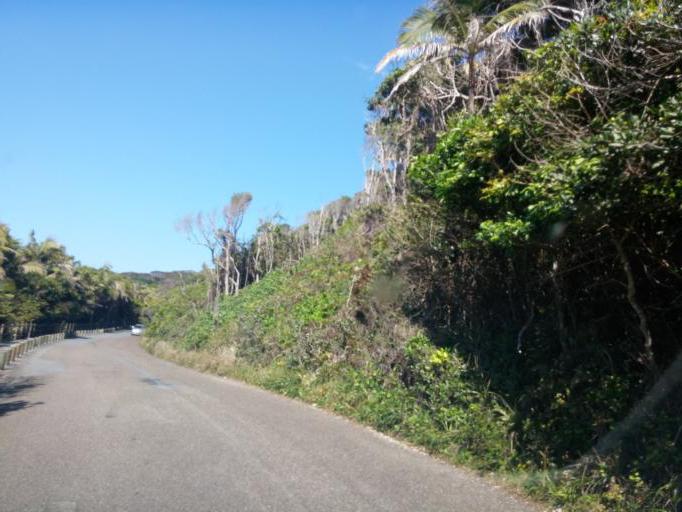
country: AU
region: New South Wales
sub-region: Port Macquarie-Hastings
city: Port Macquarie
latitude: -31.4587
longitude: 152.9326
